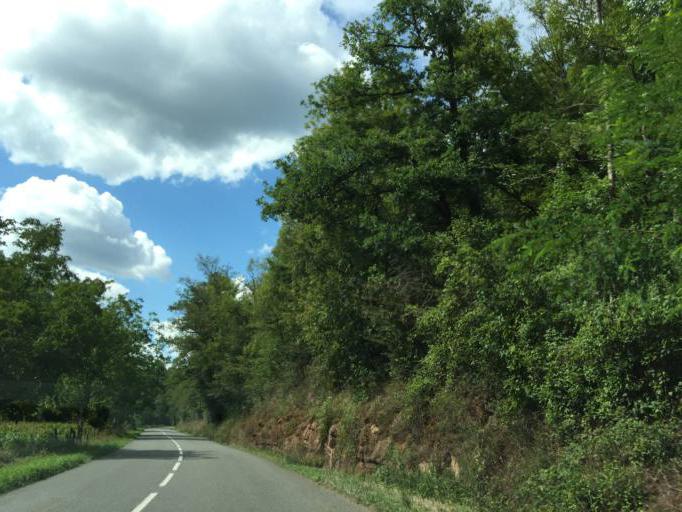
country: FR
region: Midi-Pyrenees
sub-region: Departement de l'Aveyron
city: Marcillac-Vallon
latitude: 44.4948
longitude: 2.4412
